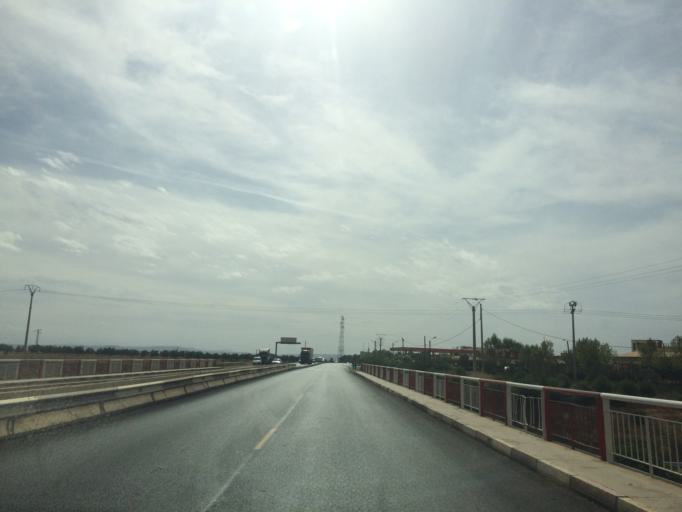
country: MA
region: Meknes-Tafilalet
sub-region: Meknes
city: Meknes
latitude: 33.8311
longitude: -5.5157
